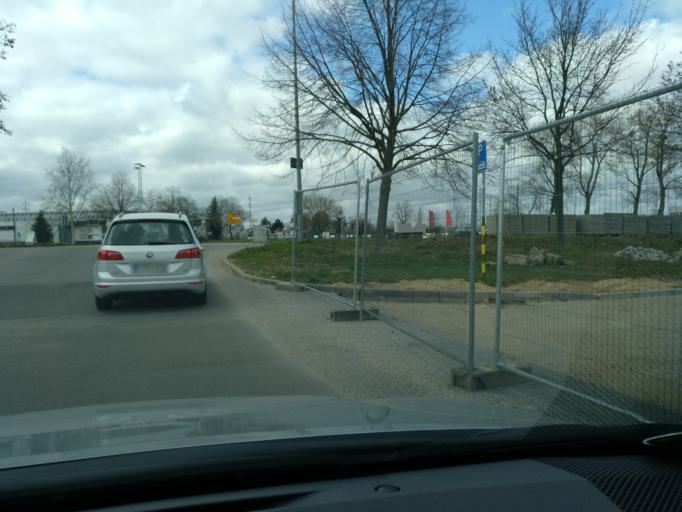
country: DE
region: Brandenburg
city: Schonefeld
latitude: 52.3889
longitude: 13.5142
